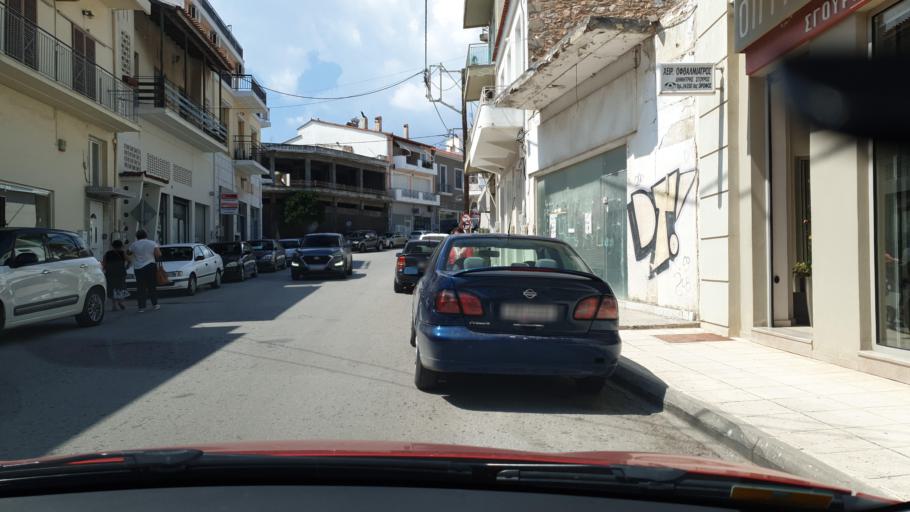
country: GR
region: Central Greece
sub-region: Nomos Evvoias
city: Aliveri
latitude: 38.4085
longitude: 24.0395
